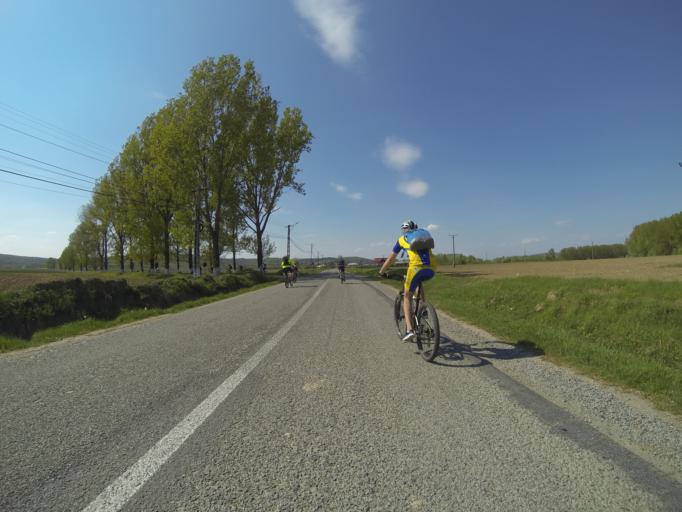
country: RO
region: Gorj
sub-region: Comuna Crusetu
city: Crusetu
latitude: 44.6209
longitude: 23.6820
